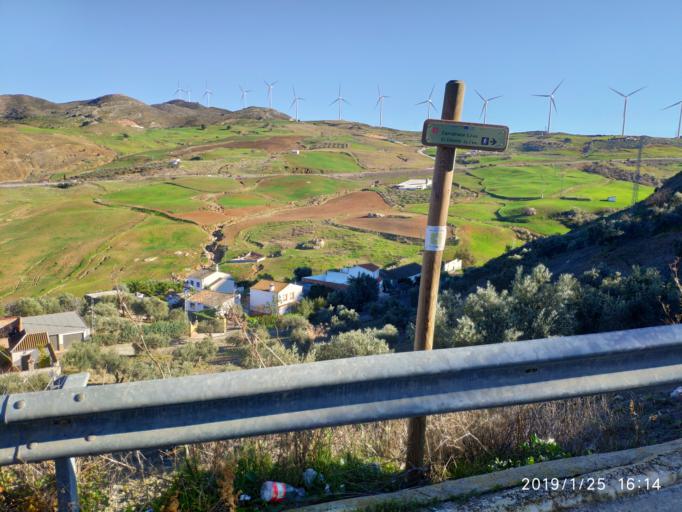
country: ES
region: Andalusia
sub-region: Provincia de Malaga
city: Ardales
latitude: 36.8757
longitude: -4.8444
